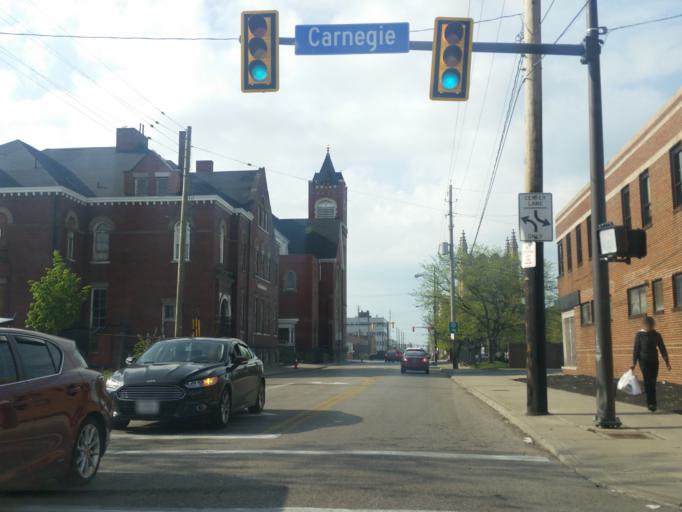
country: US
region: Ohio
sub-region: Cuyahoga County
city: Cleveland
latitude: 41.5000
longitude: -81.6668
